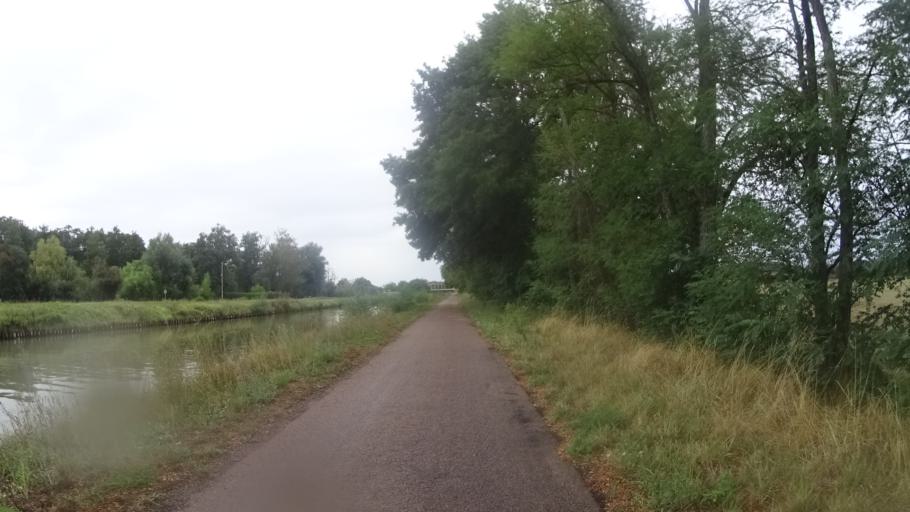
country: FR
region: Bourgogne
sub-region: Departement de la Nievre
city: Saint-Leger-des-Vignes
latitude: 46.8169
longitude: 3.3612
